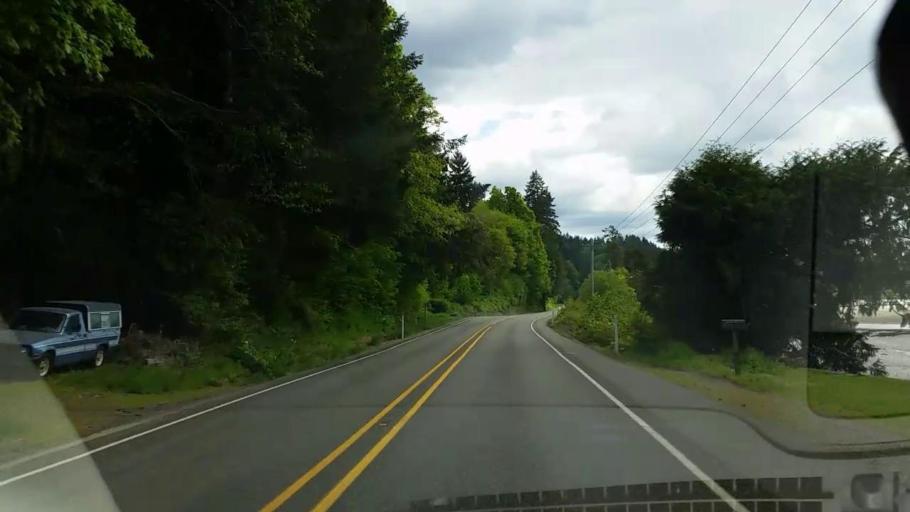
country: US
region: Washington
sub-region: Mason County
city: Shelton
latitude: 47.3446
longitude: -123.1089
